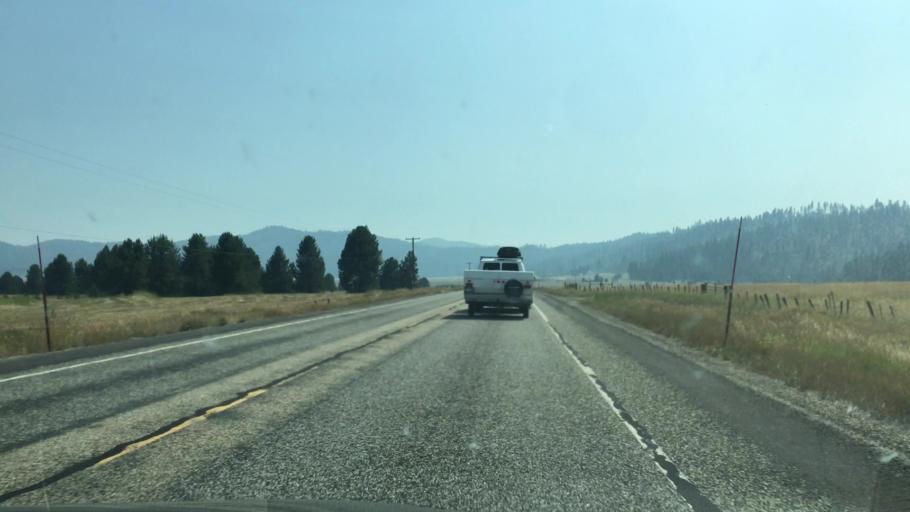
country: US
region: Idaho
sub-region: Valley County
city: Cascade
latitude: 44.3442
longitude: -116.0278
